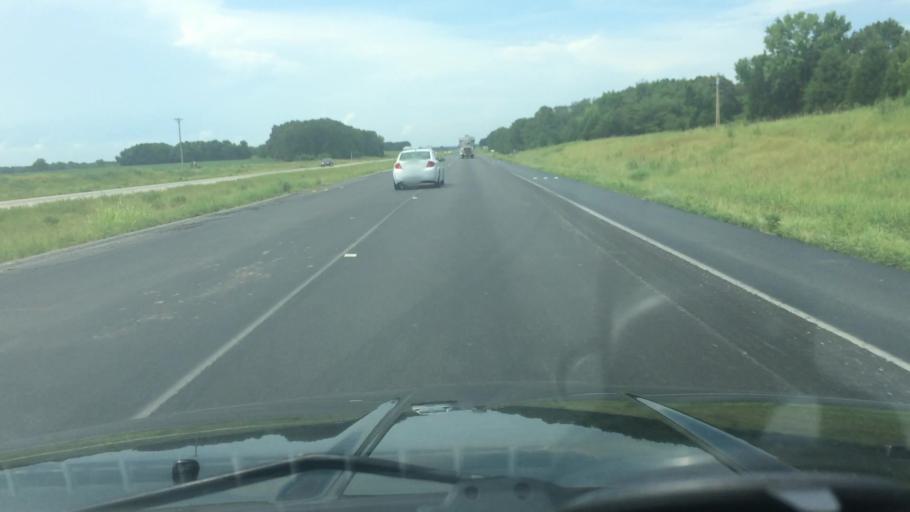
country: US
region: Missouri
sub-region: Saint Clair County
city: Osceola
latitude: 37.9665
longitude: -93.6451
